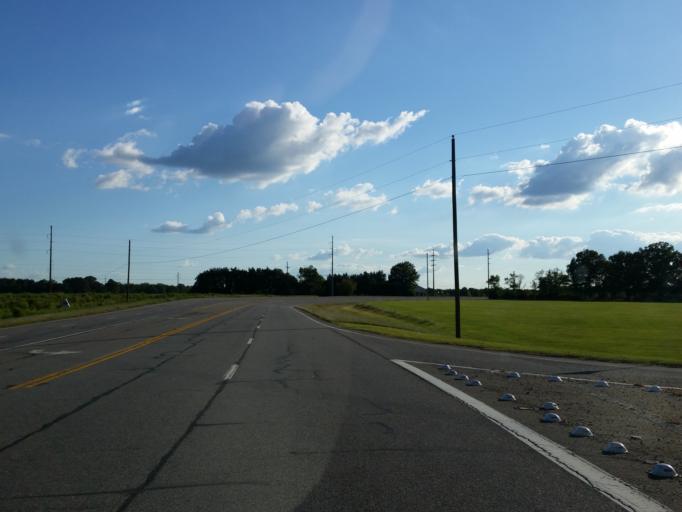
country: US
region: Georgia
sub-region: Houston County
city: Perry
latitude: 32.4923
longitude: -83.7466
